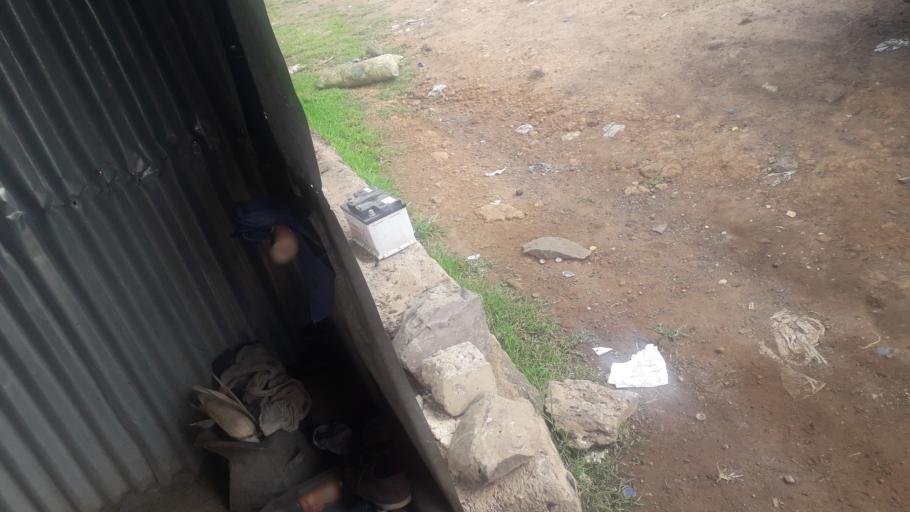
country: ET
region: Southern Nations, Nationalities, and People's Region
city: Areka
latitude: 7.4994
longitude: 37.5330
